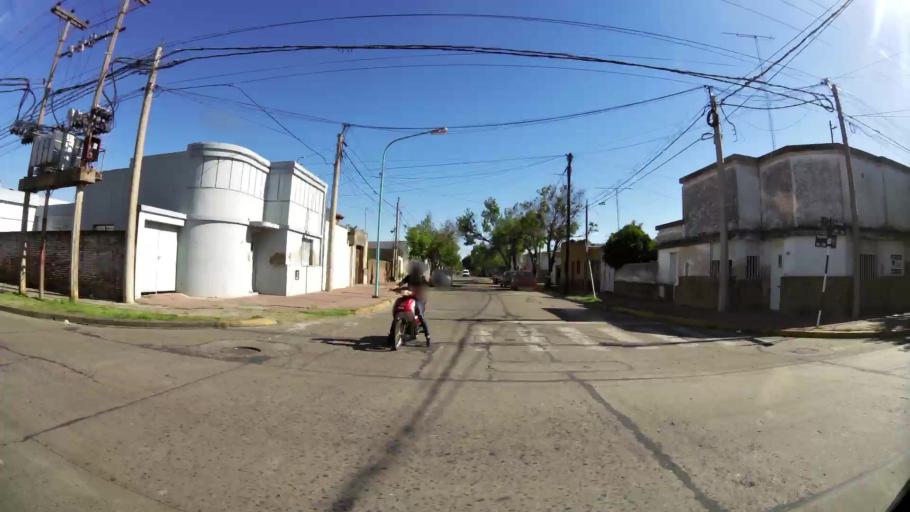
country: AR
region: Santa Fe
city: Rafaela
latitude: -31.2439
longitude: -61.4863
